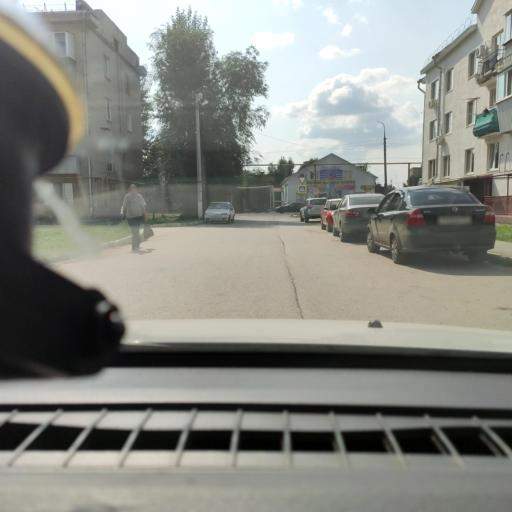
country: RU
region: Samara
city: Chapayevsk
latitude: 52.9531
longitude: 49.6880
